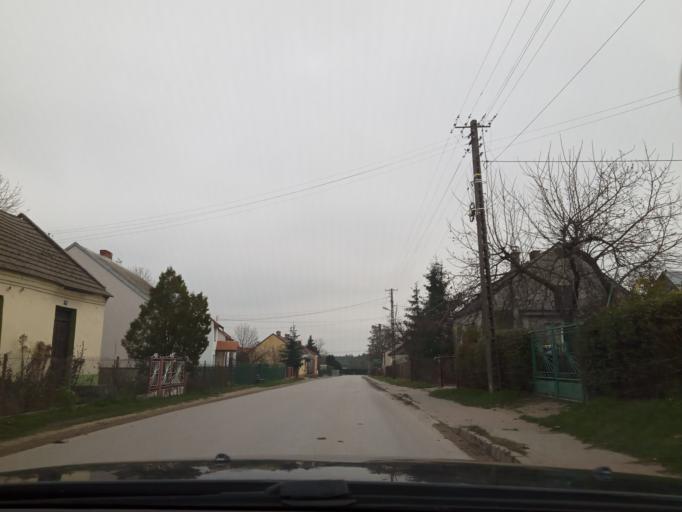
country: PL
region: Swietokrzyskie
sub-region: Powiat jedrzejowski
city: Imielno
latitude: 50.5857
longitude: 20.4471
